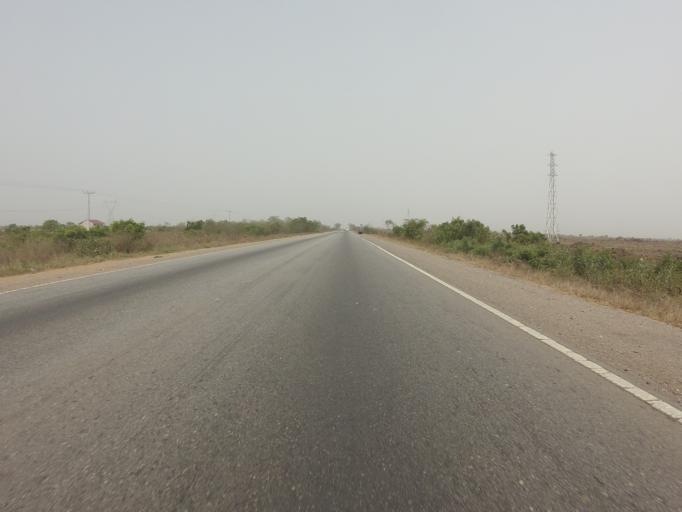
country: GH
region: Greater Accra
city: Tema
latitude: 5.7962
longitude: 0.1285
